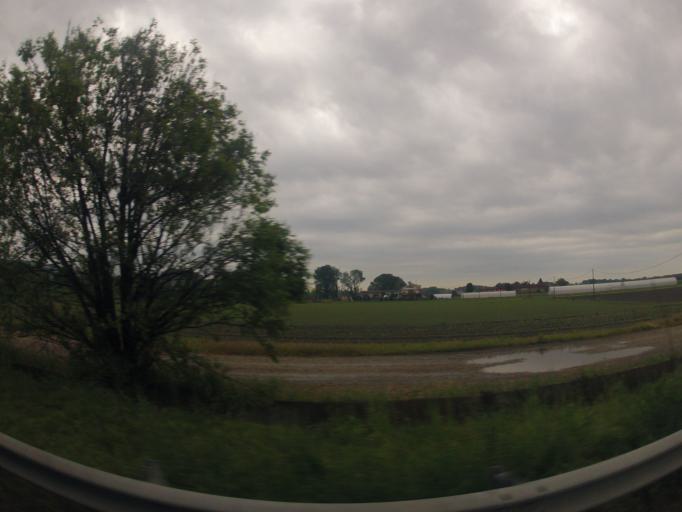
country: IT
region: Piedmont
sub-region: Provincia di Torino
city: La Loggia
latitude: 44.9602
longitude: 7.6801
